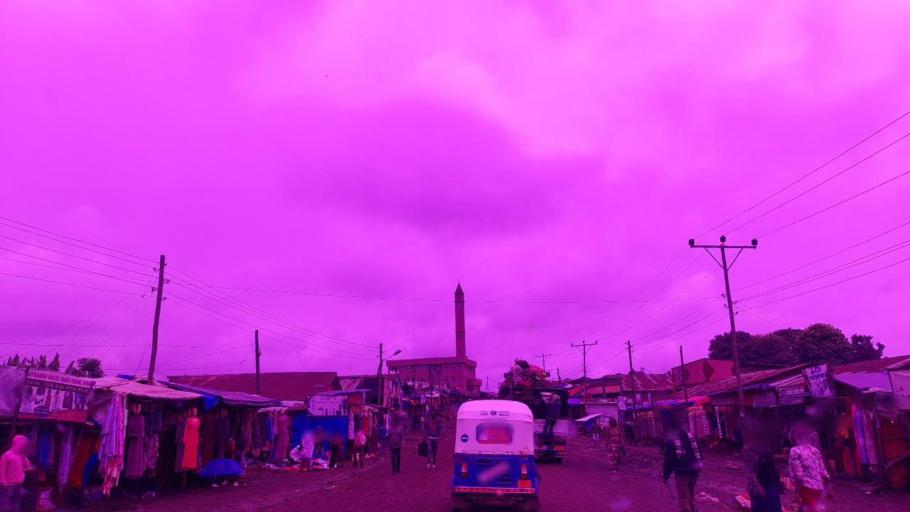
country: ET
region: Southern Nations, Nationalities, and People's Region
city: Tippi
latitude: 7.5934
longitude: 35.7569
